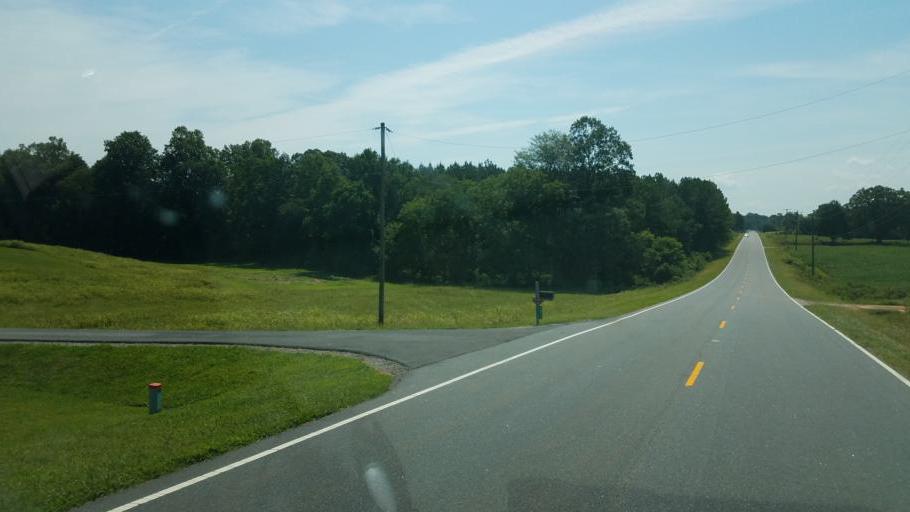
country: US
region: North Carolina
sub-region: Gaston County
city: Cherryville
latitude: 35.5260
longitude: -81.4924
